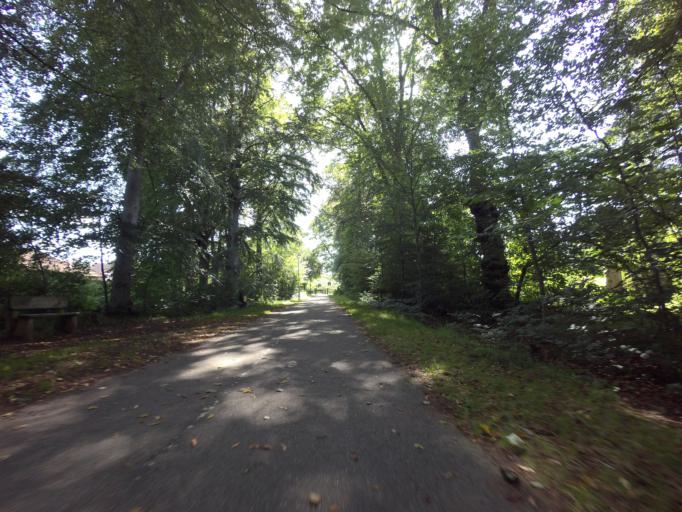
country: GB
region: Scotland
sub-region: Highland
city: Inverness
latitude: 57.4850
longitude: -4.1425
